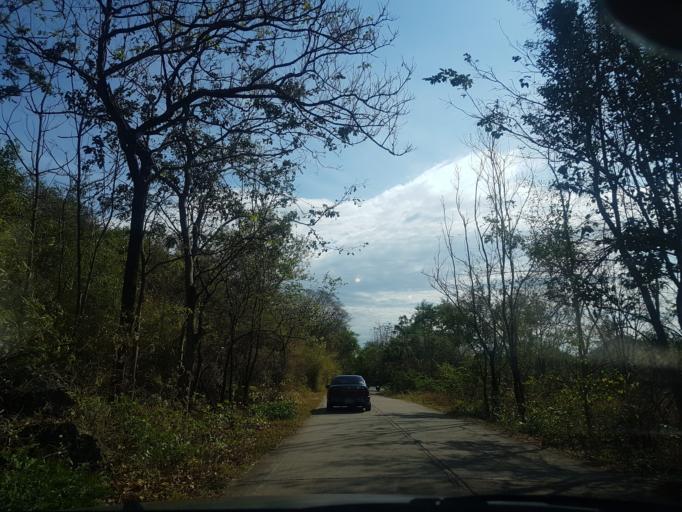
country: TH
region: Lop Buri
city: Lop Buri
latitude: 14.8229
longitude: 100.7517
